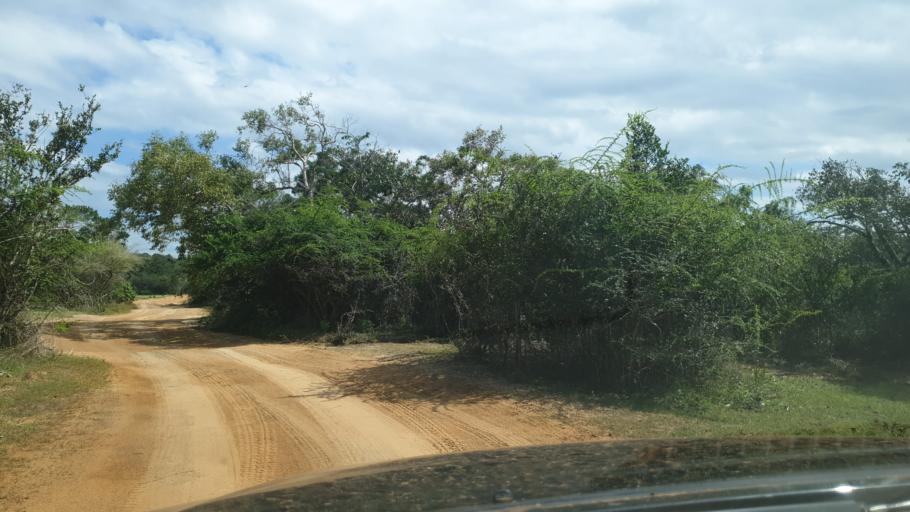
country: LK
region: North Central
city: Anuradhapura
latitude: 8.4213
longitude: 80.0093
